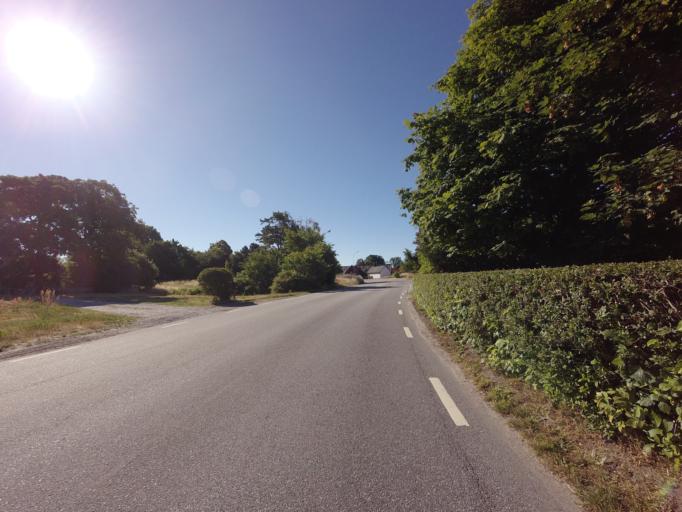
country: SE
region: Skane
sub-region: Vellinge Kommun
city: Hollviken
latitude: 55.4044
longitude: 12.9882
